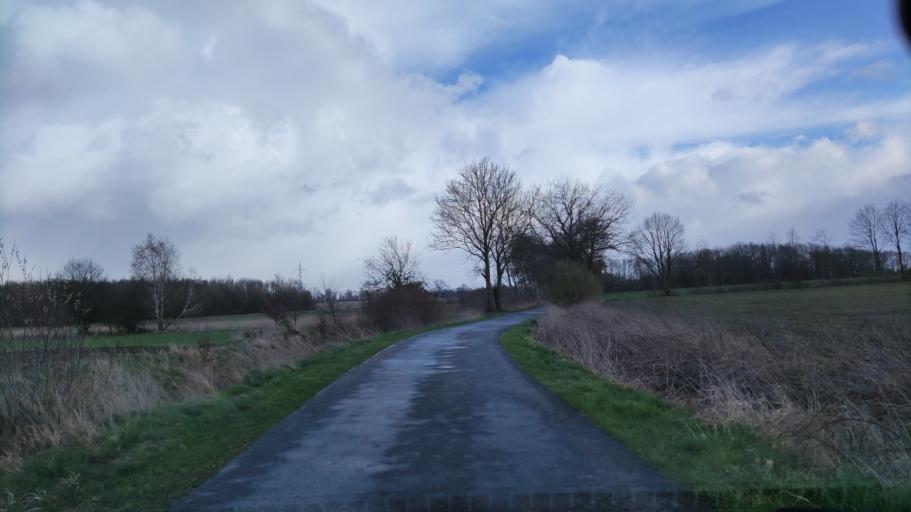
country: DE
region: Lower Saxony
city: Dahlenburg
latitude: 53.1870
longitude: 10.7148
